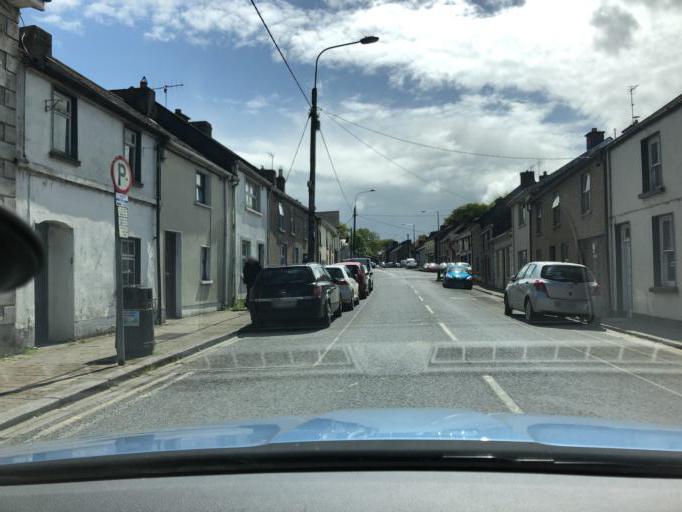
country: IE
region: Munster
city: Cashel
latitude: 52.5167
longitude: -7.8920
